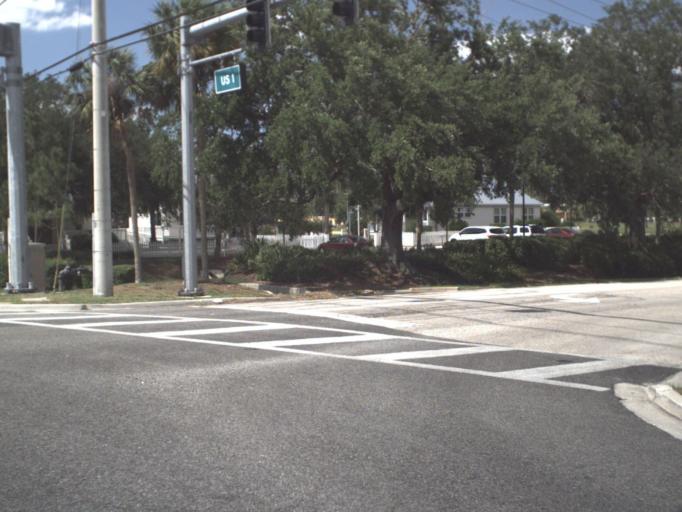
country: US
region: Florida
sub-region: Brevard County
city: Titusville
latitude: 28.6270
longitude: -80.8237
